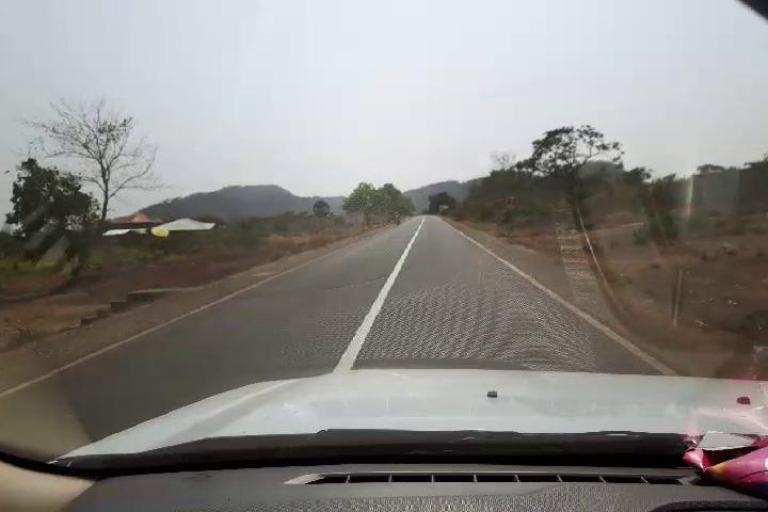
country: SL
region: Western Area
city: Waterloo
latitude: 8.2022
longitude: -13.1262
